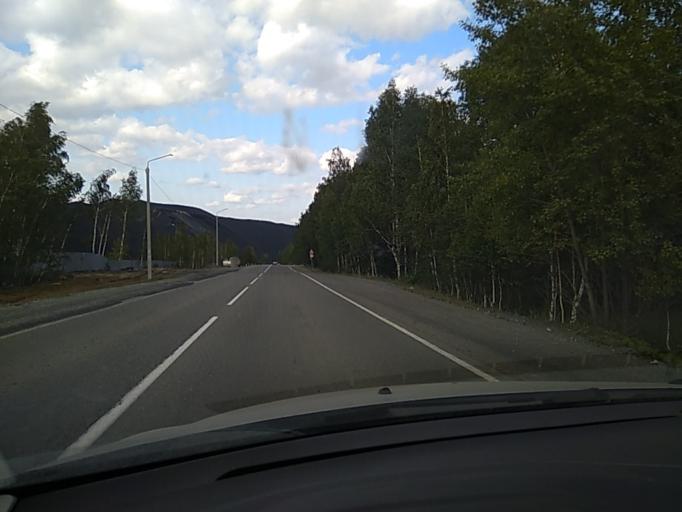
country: RU
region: Chelyabinsk
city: Karabash
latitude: 55.4930
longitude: 60.2446
